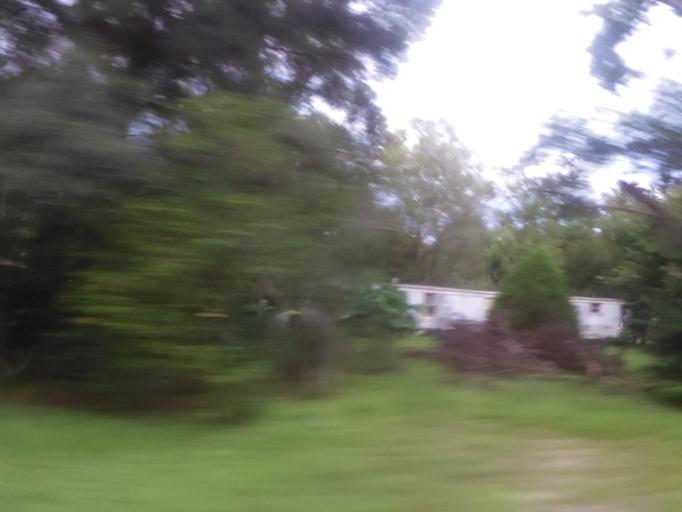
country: US
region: Florida
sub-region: Clay County
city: Bellair-Meadowbrook Terrace
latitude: 30.2842
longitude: -81.7987
